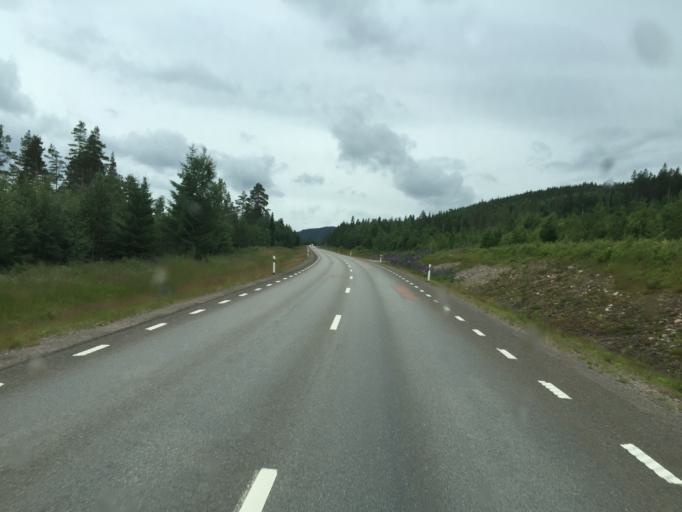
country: SE
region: Dalarna
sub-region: Malung-Saelens kommun
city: Malung
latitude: 60.6370
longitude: 13.6169
